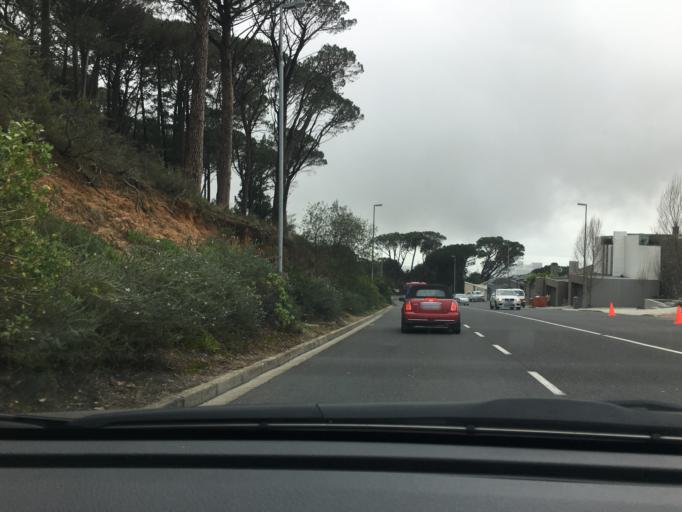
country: ZA
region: Western Cape
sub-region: City of Cape Town
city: Cape Town
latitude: -33.9412
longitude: 18.3958
